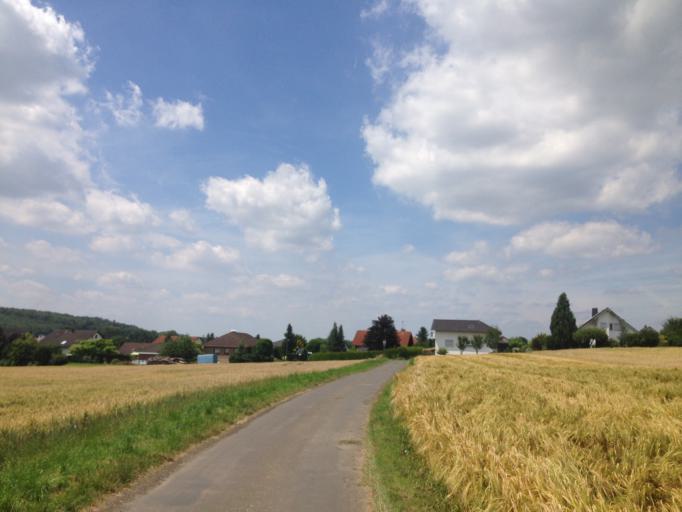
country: DE
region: Hesse
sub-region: Regierungsbezirk Giessen
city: Reiskirchen
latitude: 50.5957
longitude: 8.8600
